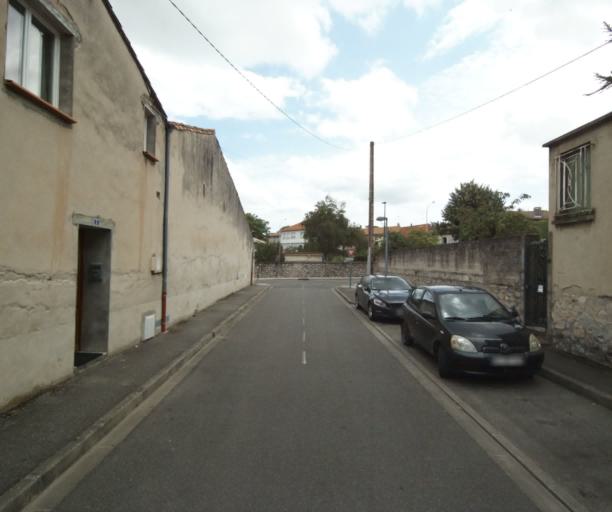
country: FR
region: Midi-Pyrenees
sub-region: Departement de la Haute-Garonne
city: Revel
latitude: 43.4564
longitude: 1.9999
